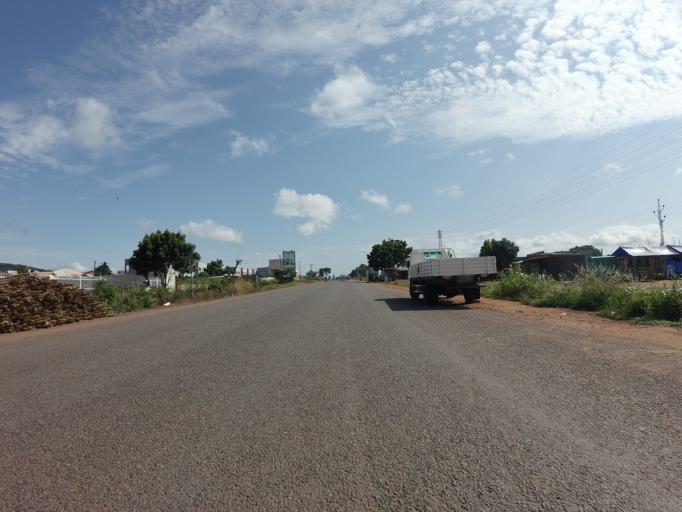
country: GH
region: Eastern
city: Aburi
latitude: 5.7911
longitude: -0.1300
